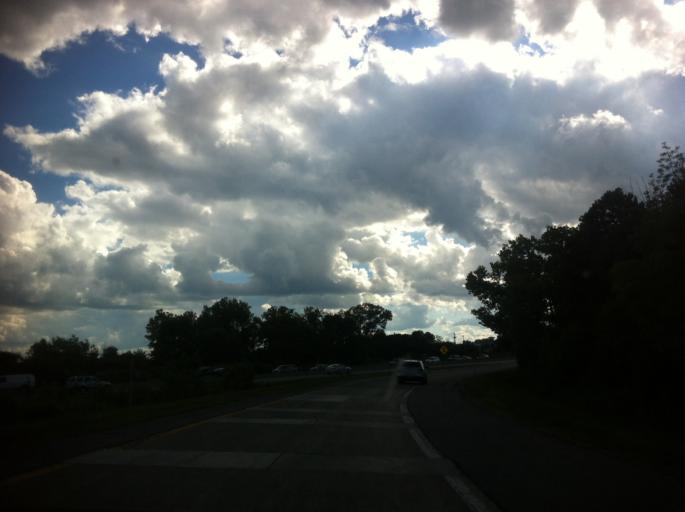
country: US
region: Michigan
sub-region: Washtenaw County
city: Ann Arbor
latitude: 42.2379
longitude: -83.7409
